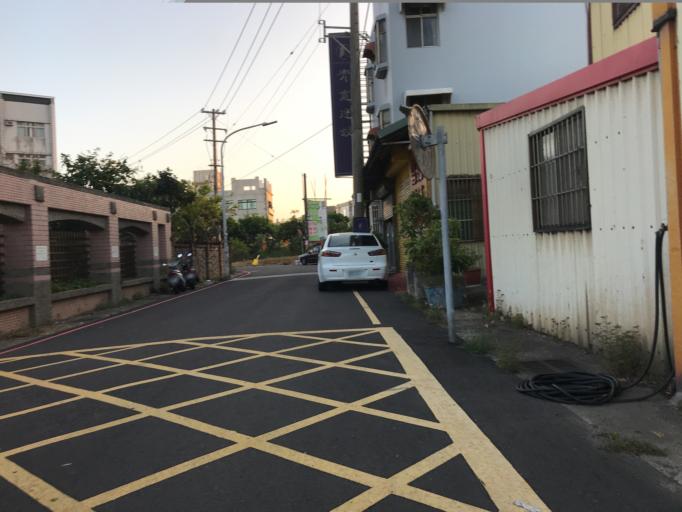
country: TW
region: Taiwan
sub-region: Hsinchu
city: Hsinchu
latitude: 24.8075
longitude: 120.9405
